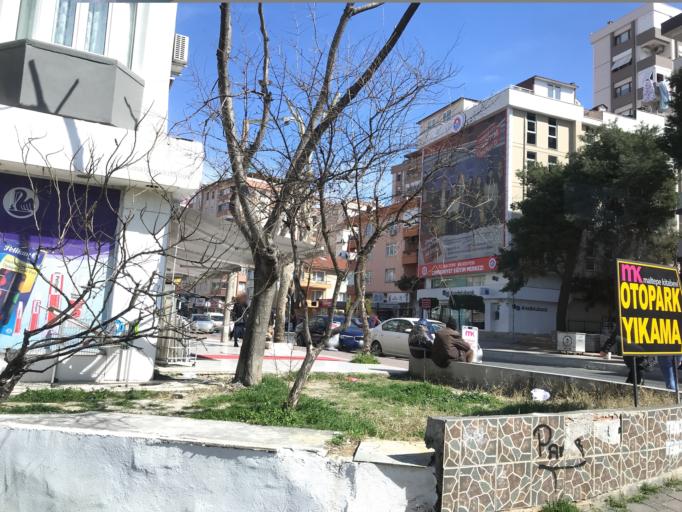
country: TR
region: Istanbul
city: Maltepe
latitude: 40.9276
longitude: 29.1336
